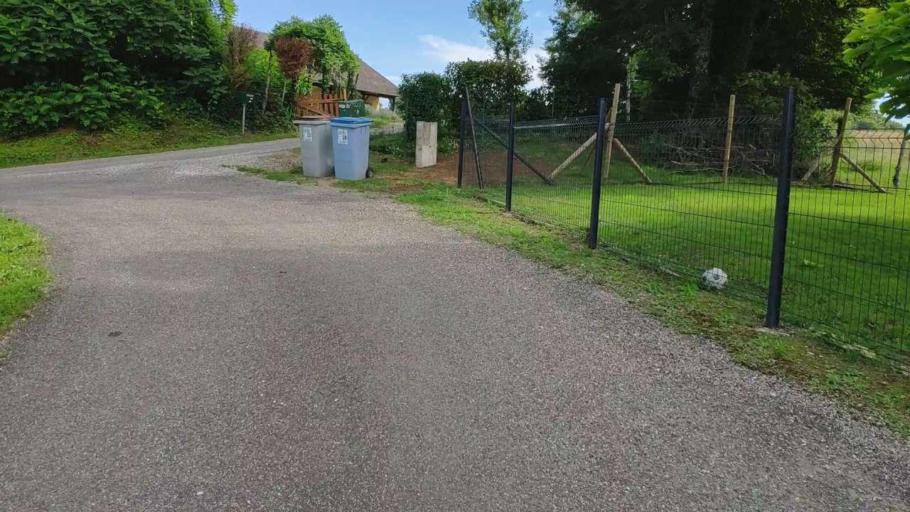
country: FR
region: Franche-Comte
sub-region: Departement du Jura
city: Bletterans
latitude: 46.8230
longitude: 5.5365
